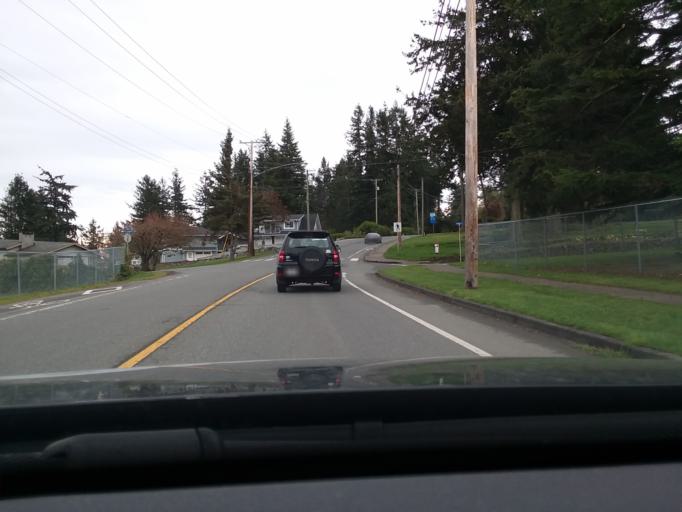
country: CA
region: British Columbia
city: North Saanich
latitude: 48.6194
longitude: -123.4168
